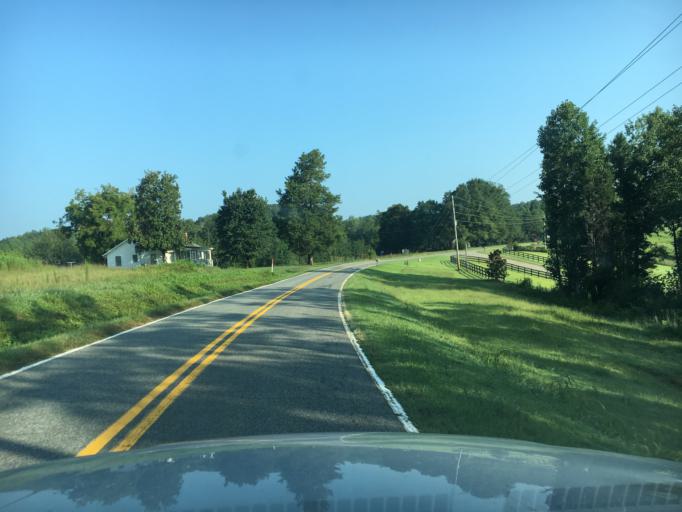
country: US
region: North Carolina
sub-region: Rutherford County
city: Rutherfordton
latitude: 35.2667
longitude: -82.0316
